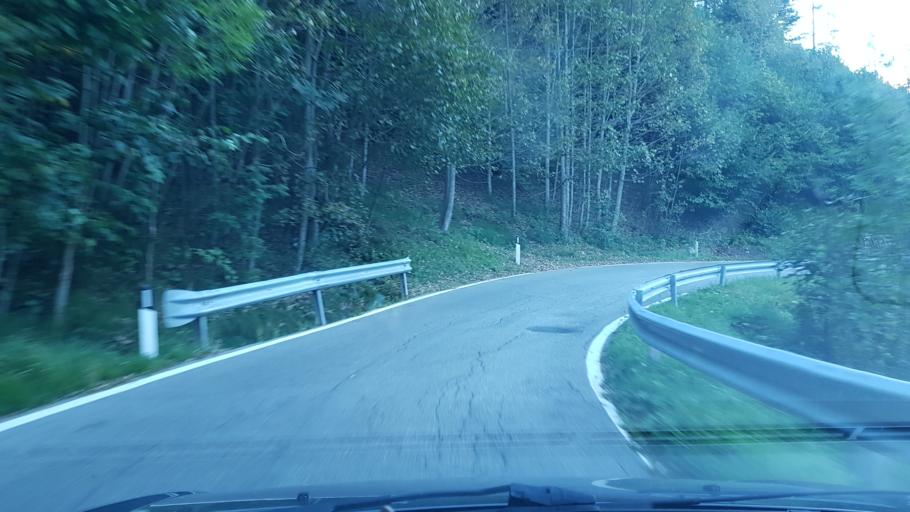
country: IT
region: Veneto
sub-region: Provincia di Belluno
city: Fusine
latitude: 46.3445
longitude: 12.1113
